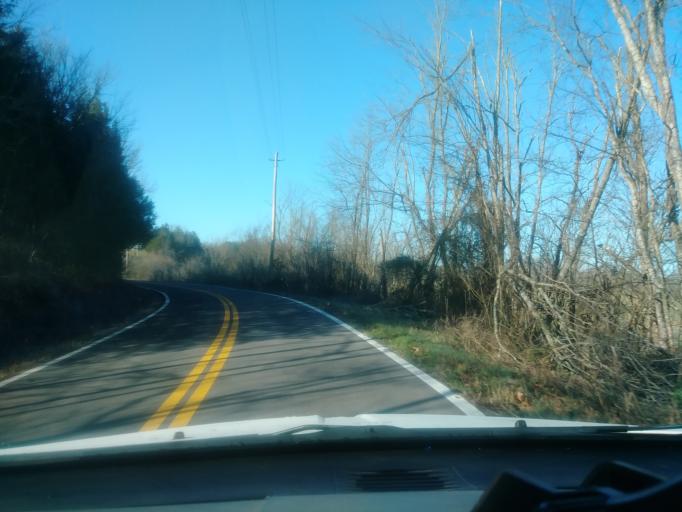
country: US
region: Tennessee
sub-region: Greene County
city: Mosheim
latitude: 36.1219
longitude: -83.0646
